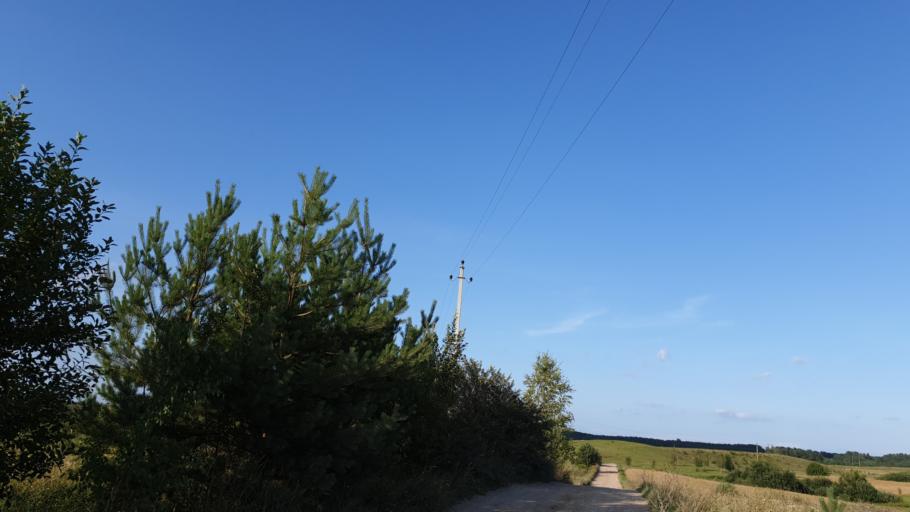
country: LT
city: Grigiskes
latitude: 54.7691
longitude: 25.0275
